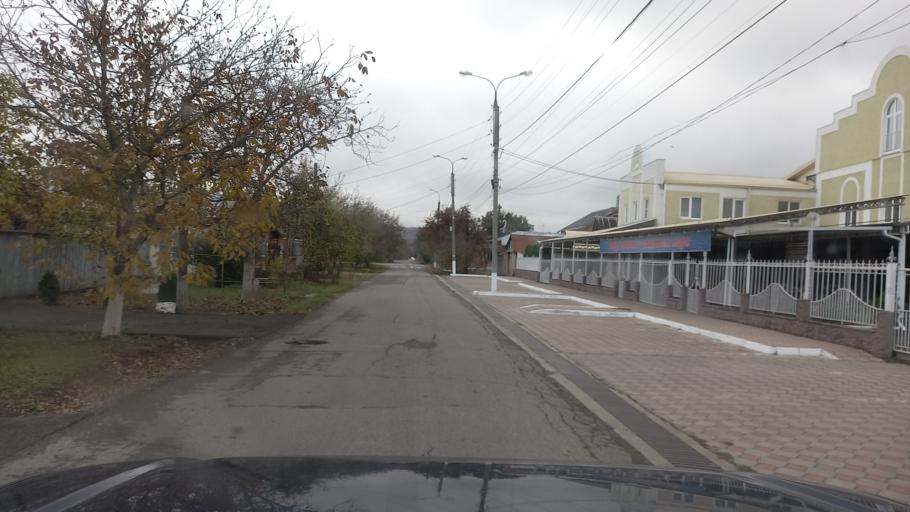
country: RU
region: Adygeya
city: Maykop
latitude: 44.6065
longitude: 40.0841
